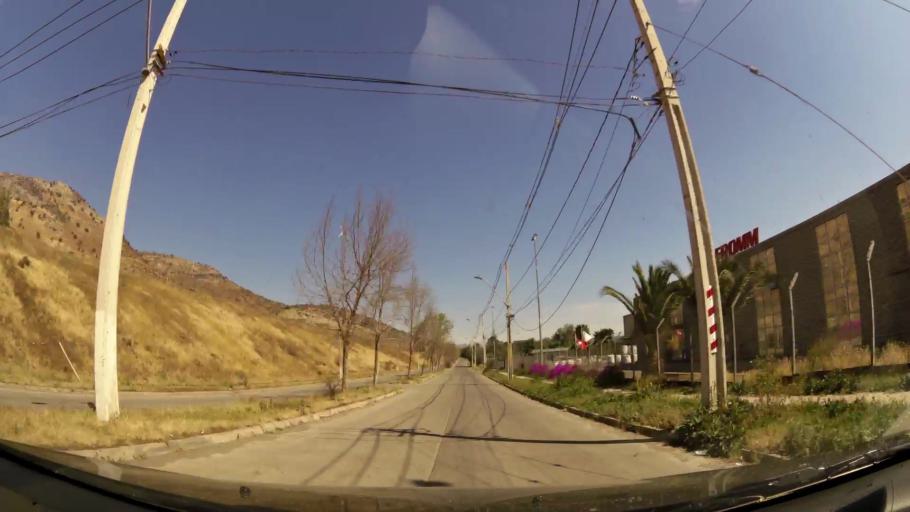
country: CL
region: Santiago Metropolitan
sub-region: Provincia de Santiago
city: Lo Prado
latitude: -33.3810
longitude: -70.7400
